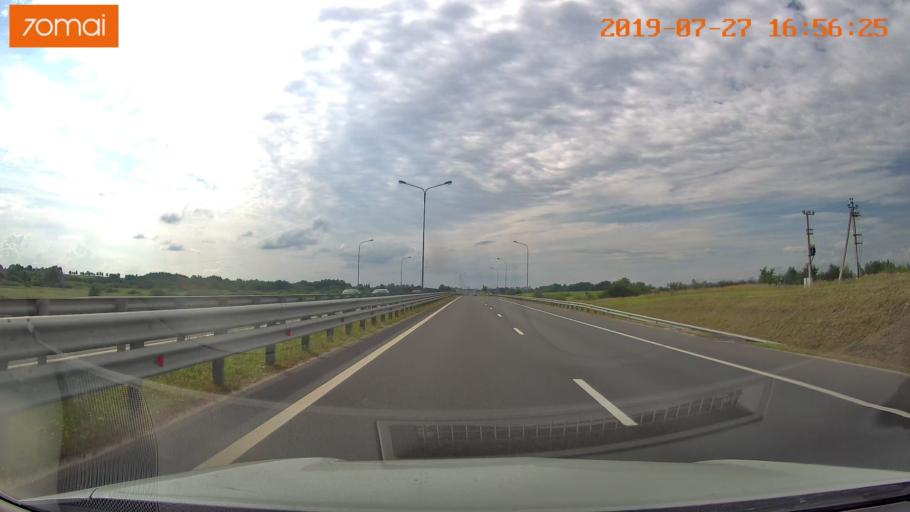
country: RU
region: Kaliningrad
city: Bol'shoe Isakovo
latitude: 54.6948
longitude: 20.7402
